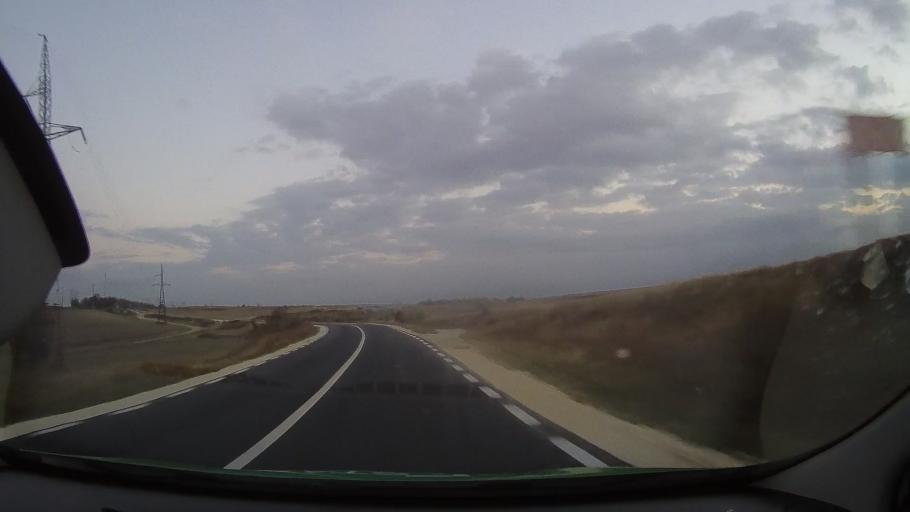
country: RO
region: Constanta
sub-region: Comuna Baneasa
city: Baneasa
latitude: 44.0816
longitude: 27.6889
